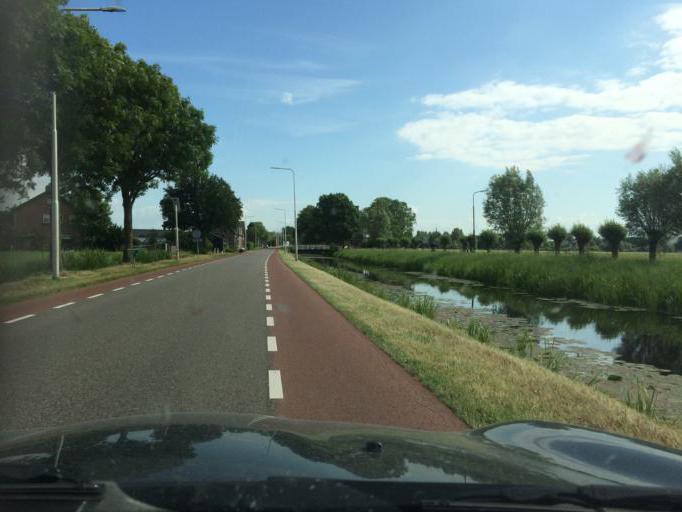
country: NL
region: Utrecht
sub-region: Gemeente Woerden
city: Woerden
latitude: 52.1012
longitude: 4.8945
